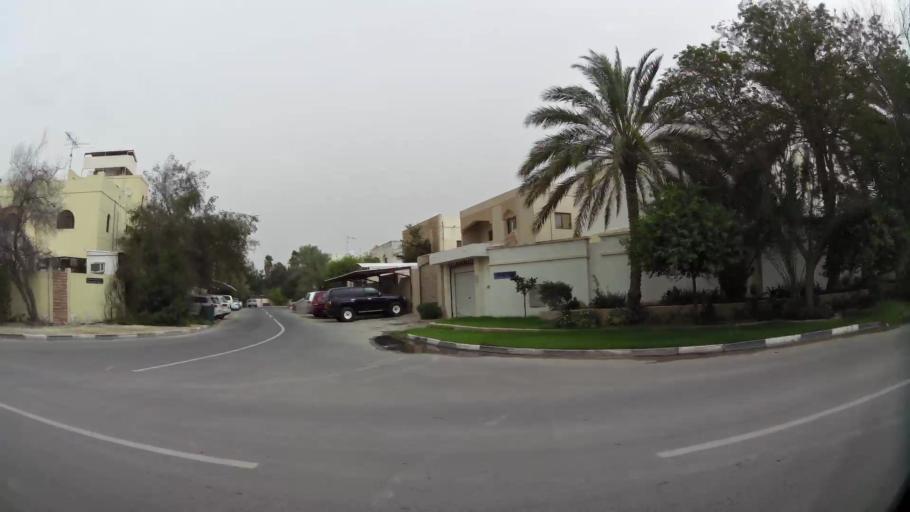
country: QA
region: Baladiyat ad Dawhah
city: Doha
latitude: 25.2413
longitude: 51.5214
